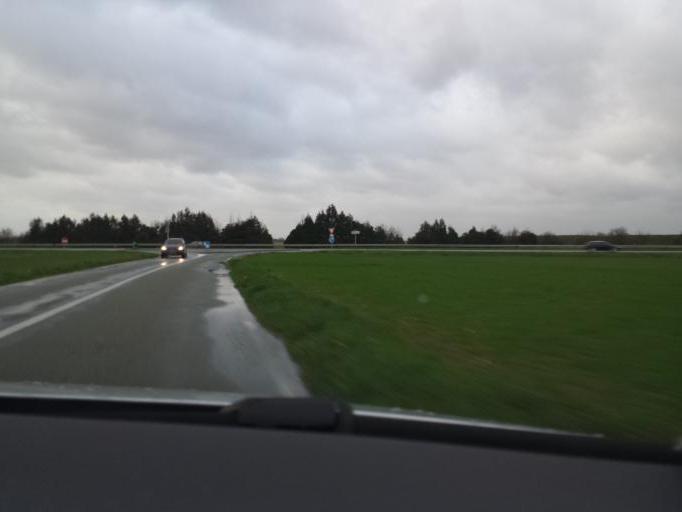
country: FR
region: Haute-Normandie
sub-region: Departement de l'Eure
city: Gravigny
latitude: 49.0137
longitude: 1.2138
